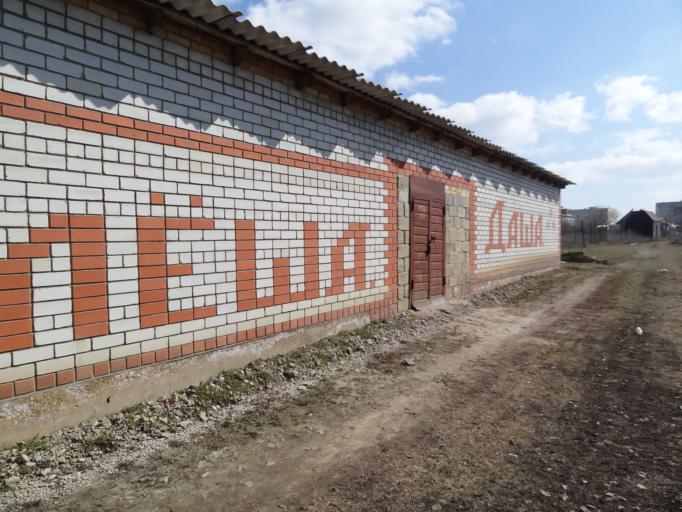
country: RU
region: Saratov
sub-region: Saratovskiy Rayon
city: Saratov
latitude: 51.6674
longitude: 46.0573
